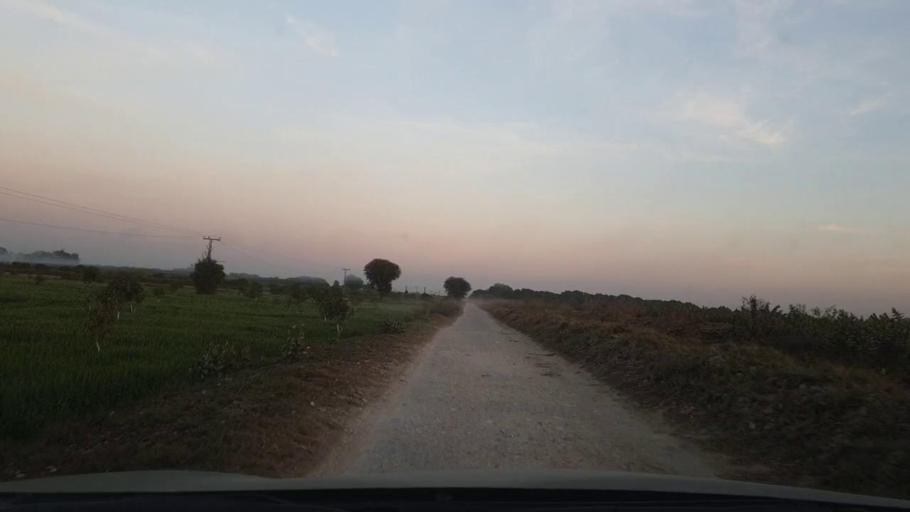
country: PK
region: Sindh
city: Tando Allahyar
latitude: 25.5630
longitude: 68.7664
